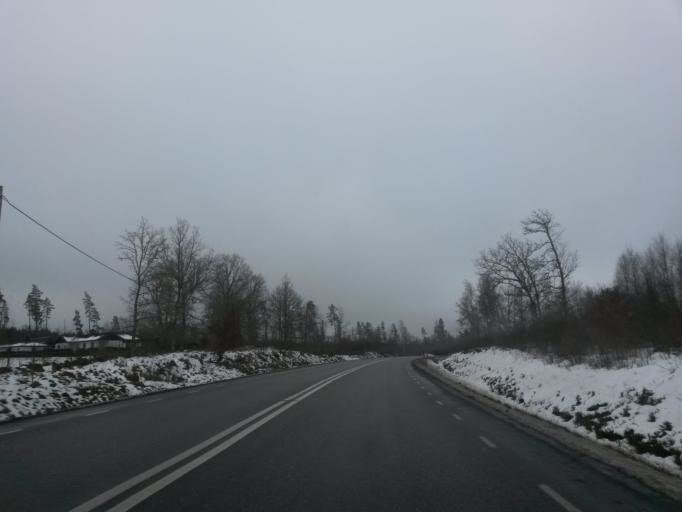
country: SE
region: Vaestra Goetaland
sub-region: Vargarda Kommun
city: Vargarda
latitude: 58.0139
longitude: 12.8181
